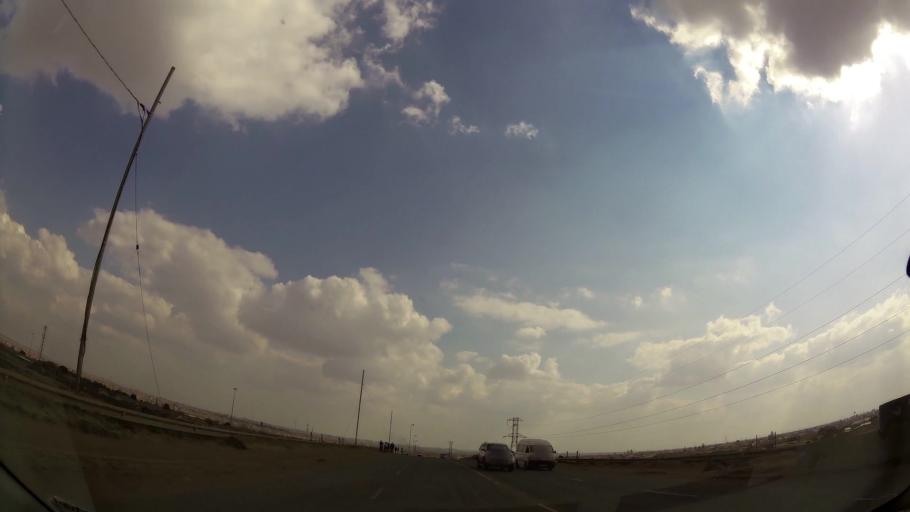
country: ZA
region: Gauteng
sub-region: Ekurhuleni Metropolitan Municipality
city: Springs
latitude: -26.1179
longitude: 28.4693
